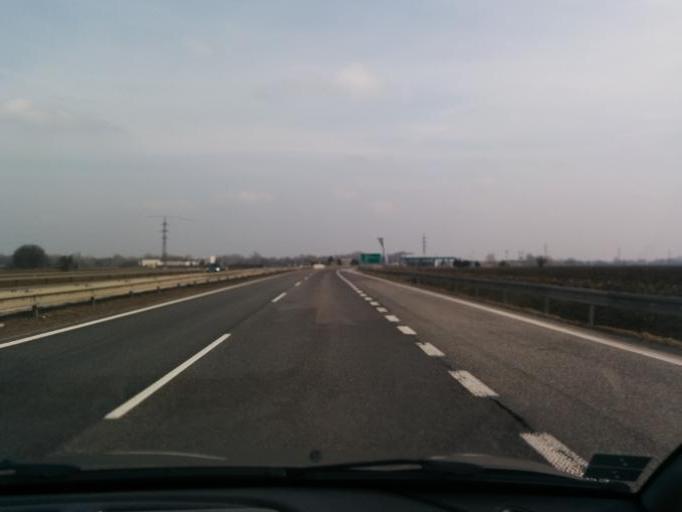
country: SK
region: Trnavsky
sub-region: Okres Galanta
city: Galanta
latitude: 48.2587
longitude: 17.7499
